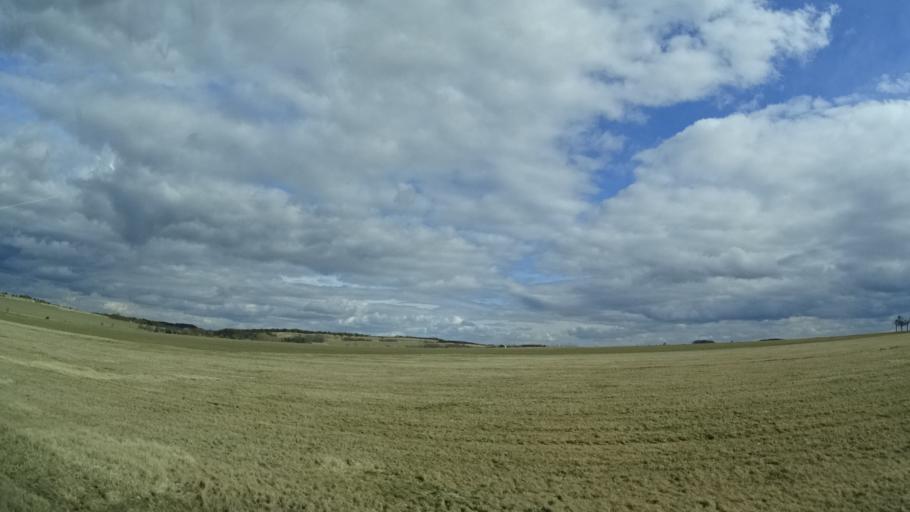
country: DE
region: Thuringia
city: Blankenhain
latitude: 50.8352
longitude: 11.3420
